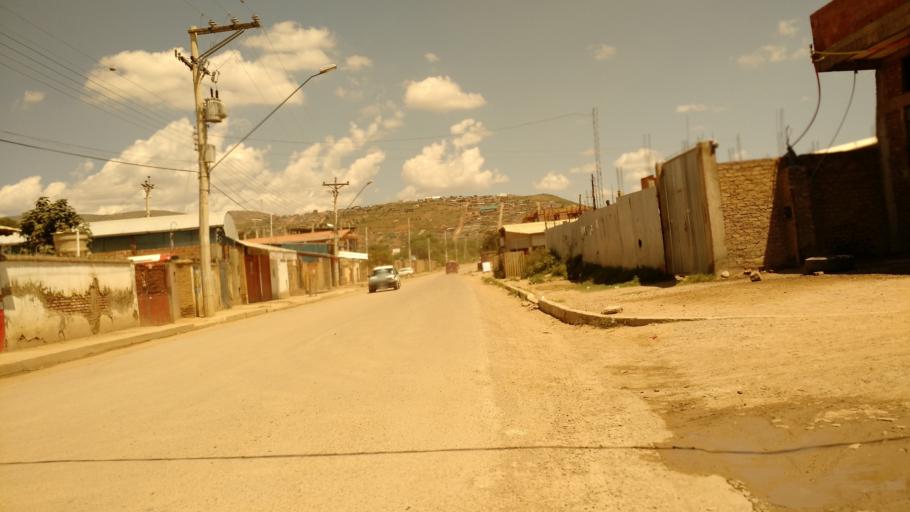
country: BO
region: Cochabamba
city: Cochabamba
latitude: -17.4522
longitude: -66.1559
